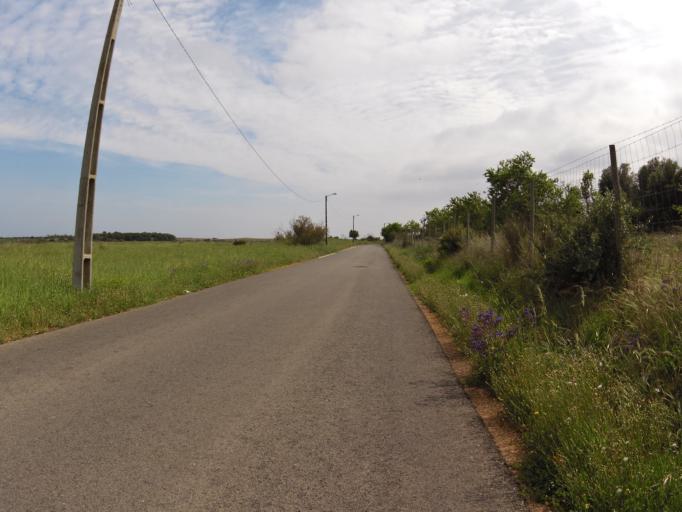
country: PT
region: Faro
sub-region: Silves
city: Armacao de Pera
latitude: 37.1100
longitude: -8.3493
